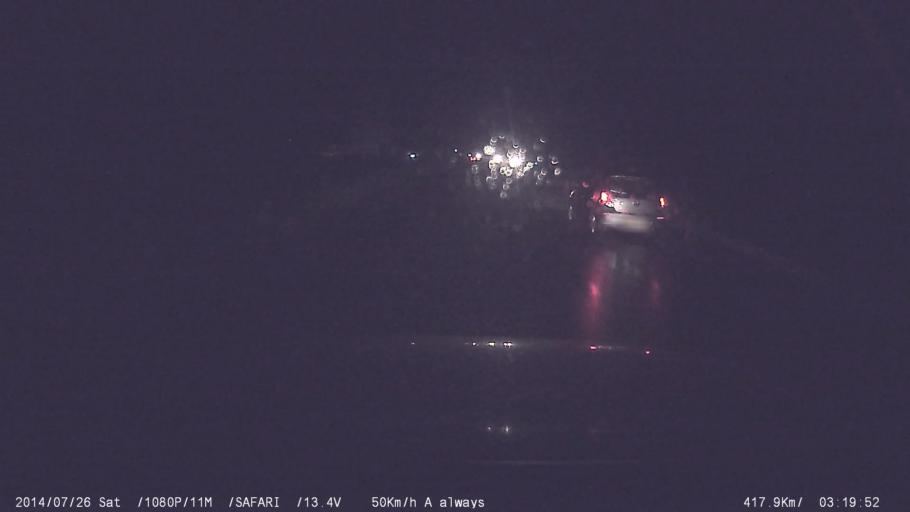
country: IN
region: Kerala
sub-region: Palakkad district
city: Palakkad
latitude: 10.6443
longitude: 76.5418
